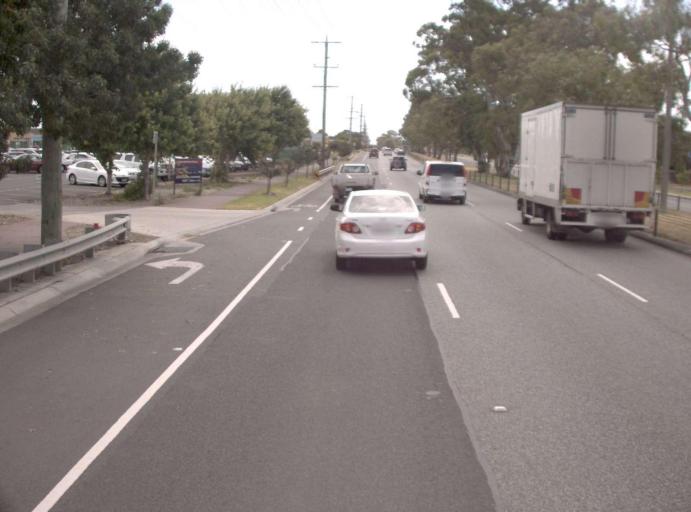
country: AU
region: Victoria
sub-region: Greater Dandenong
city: Keysborough
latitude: -37.9937
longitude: 145.1681
